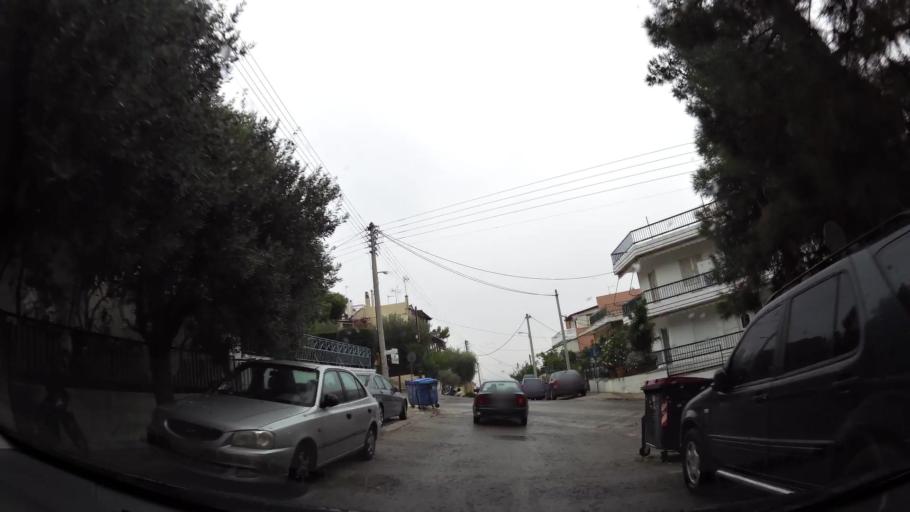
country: GR
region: Attica
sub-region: Nomarchia Athinas
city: Chaidari
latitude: 38.0055
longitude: 23.6572
